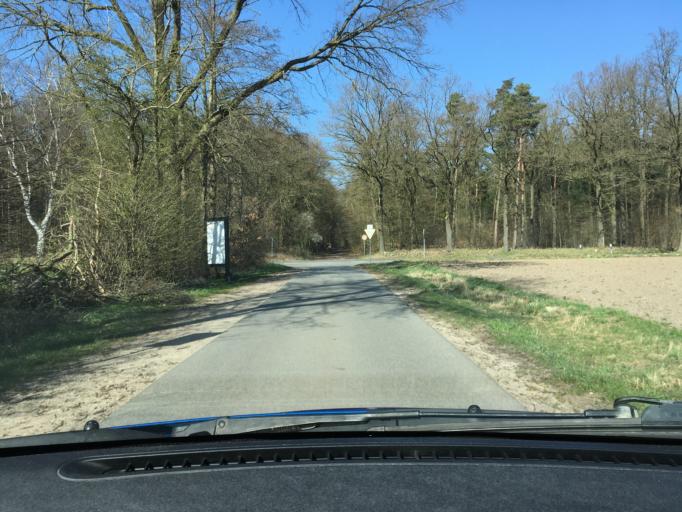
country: DE
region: Lower Saxony
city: Schwienau
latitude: 53.0302
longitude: 10.4443
